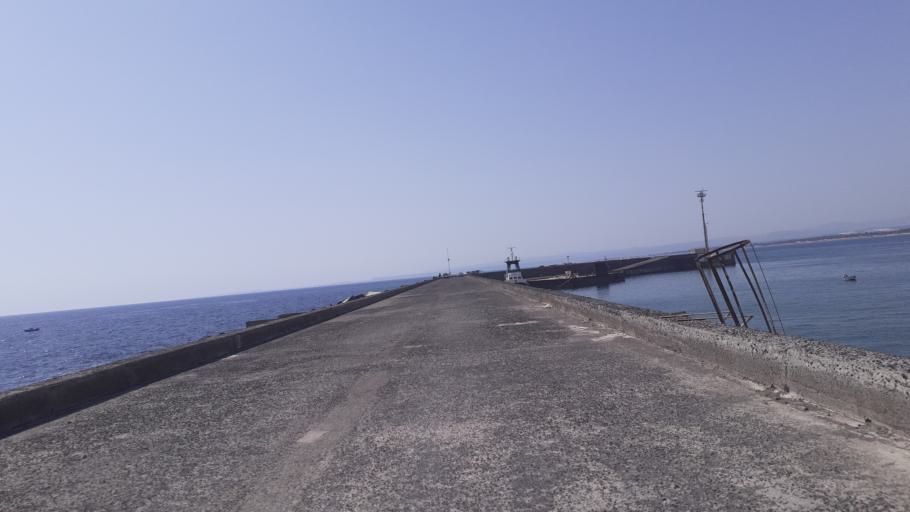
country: IT
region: Sicily
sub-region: Catania
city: Catania
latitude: 37.4905
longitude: 15.0999
